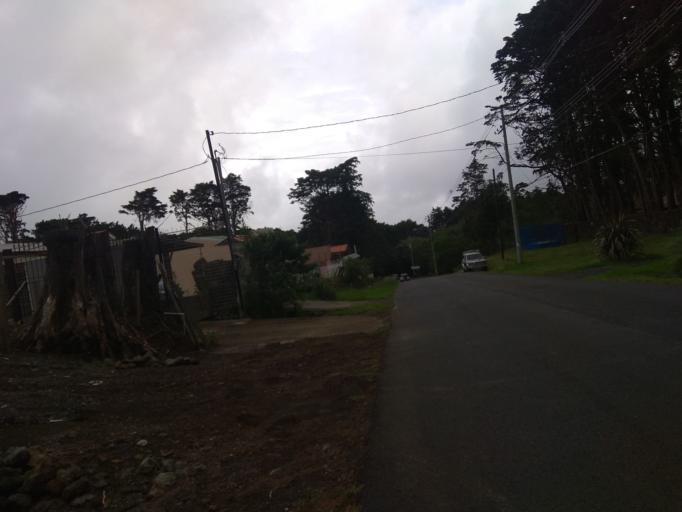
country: CR
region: Heredia
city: San Josecito
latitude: 10.0662
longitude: -84.0848
